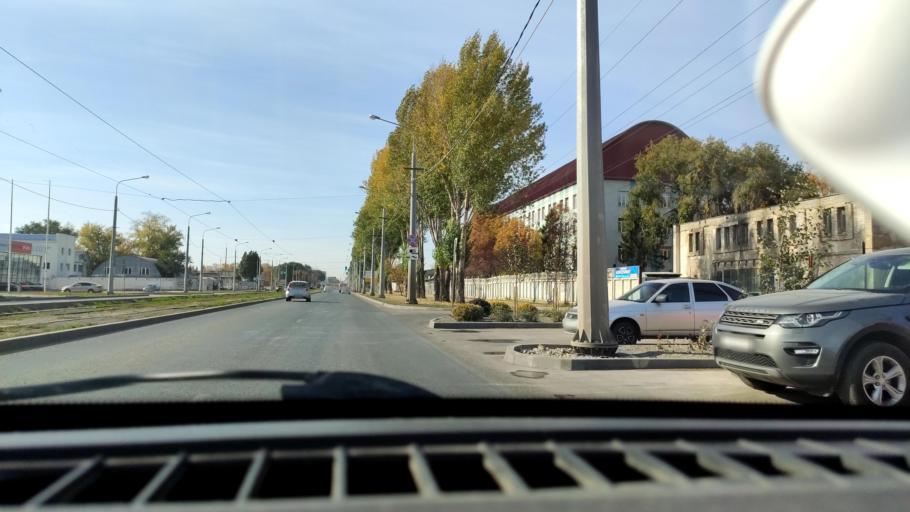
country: RU
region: Samara
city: Samara
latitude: 53.2001
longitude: 50.2583
